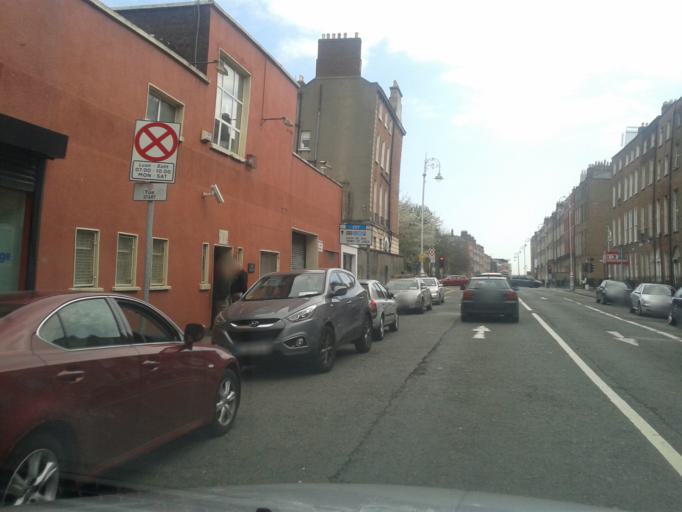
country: IE
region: Leinster
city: Drumcondra
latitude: 53.3575
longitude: -6.2597
